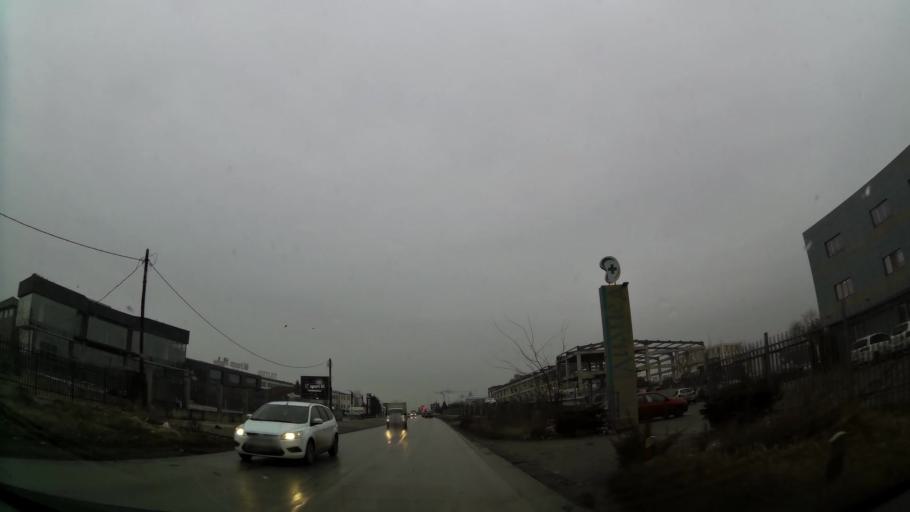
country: MK
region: Suto Orizari
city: Suto Orizare
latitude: 42.0416
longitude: 21.3932
